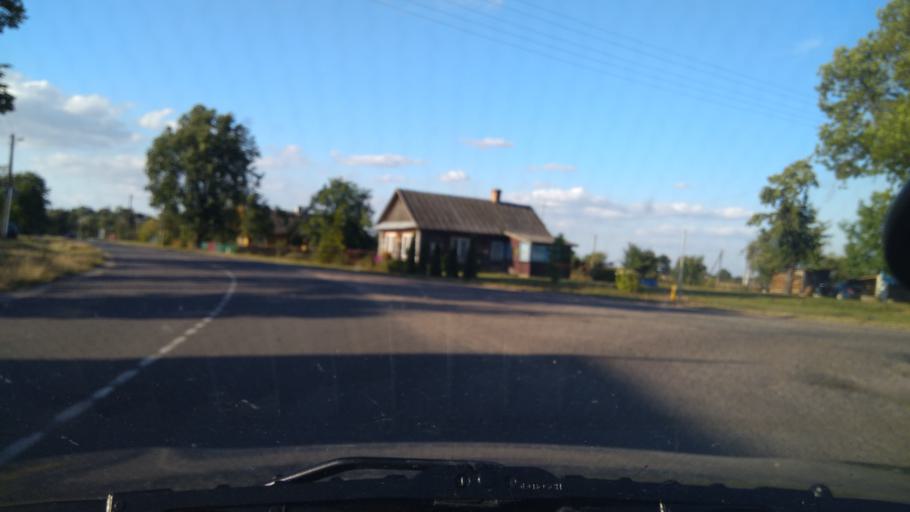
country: BY
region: Brest
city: Byaroza
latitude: 52.5889
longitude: 24.8703
